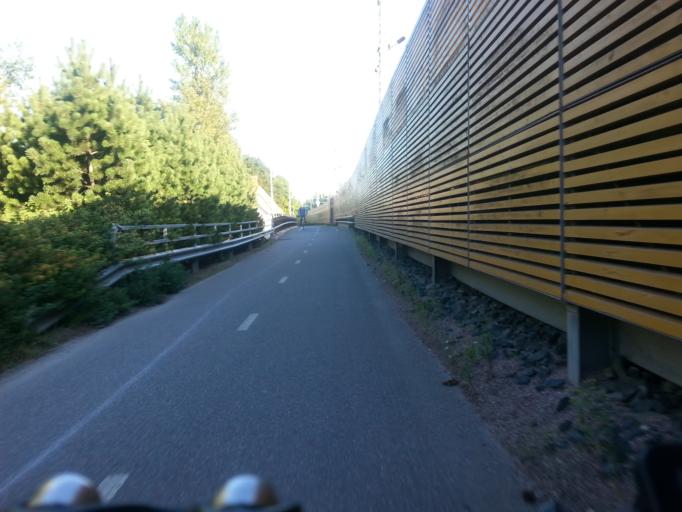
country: FI
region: Uusimaa
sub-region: Helsinki
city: Helsinki
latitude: 60.2168
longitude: 24.8983
